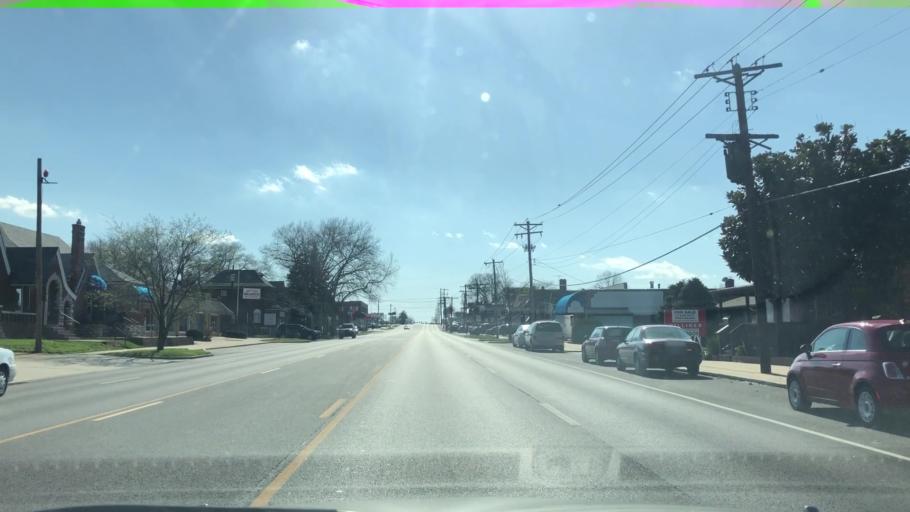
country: US
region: Missouri
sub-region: Saint Louis County
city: Saint George
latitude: 38.5569
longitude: -90.3080
